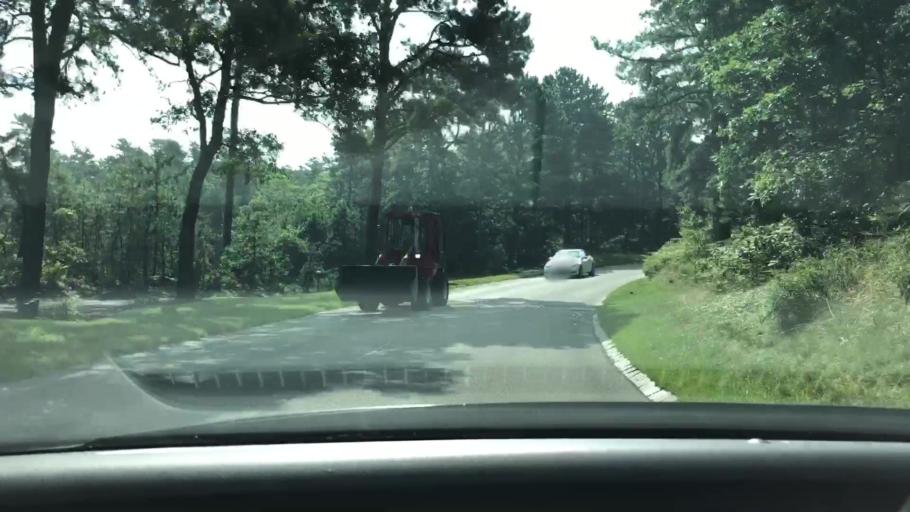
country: US
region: Massachusetts
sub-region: Plymouth County
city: White Island Shores
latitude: 41.8823
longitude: -70.6006
